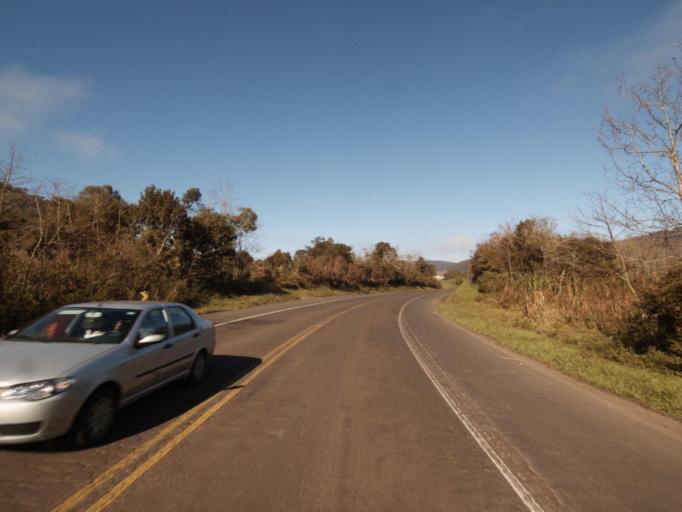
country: BR
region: Rio Grande do Sul
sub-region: Frederico Westphalen
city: Frederico Westphalen
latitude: -26.9917
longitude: -53.2258
